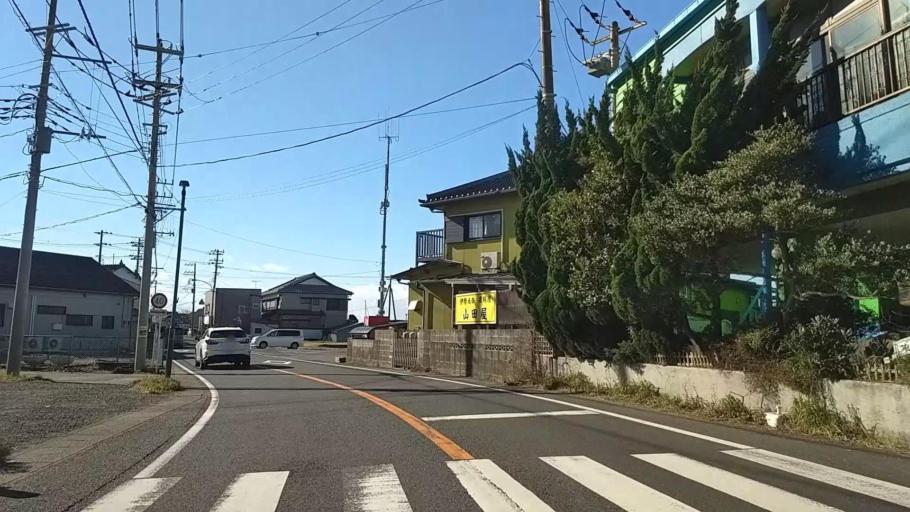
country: JP
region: Chiba
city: Tateyama
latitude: 35.1369
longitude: 139.8384
